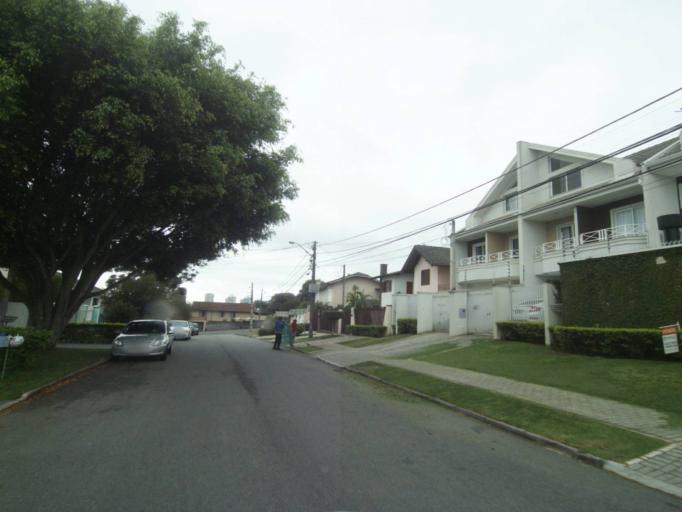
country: BR
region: Parana
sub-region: Curitiba
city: Curitiba
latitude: -25.4249
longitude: -49.3426
